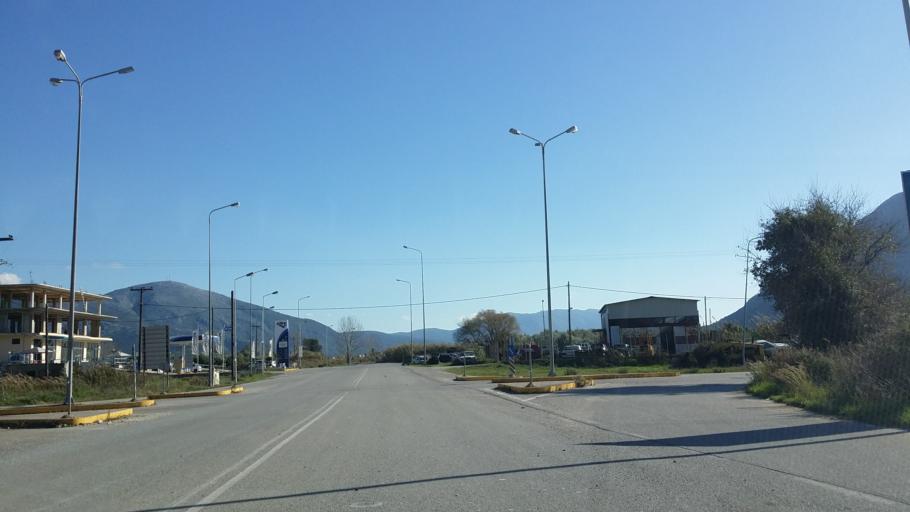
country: GR
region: West Greece
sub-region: Nomos Aitolias kai Akarnanias
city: Kandila
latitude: 38.6764
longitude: 20.9399
